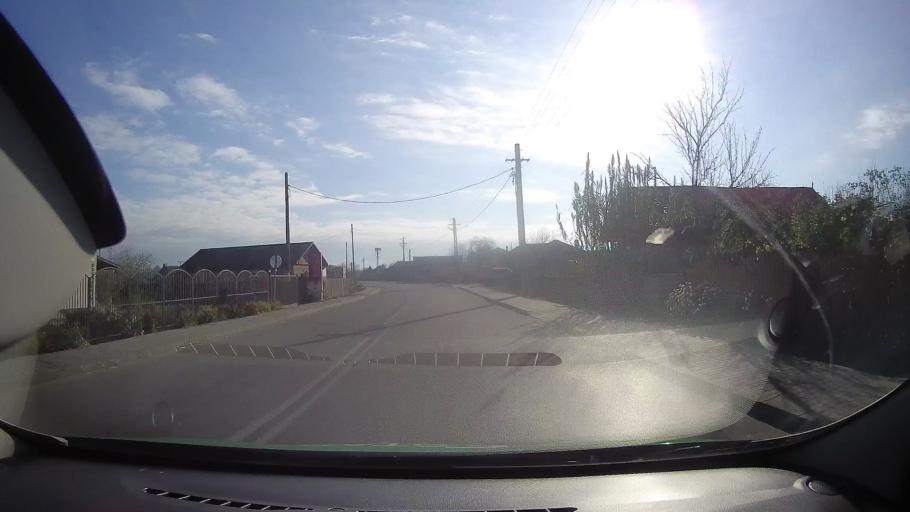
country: RO
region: Tulcea
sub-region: Comuna Murighiol
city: Murighiol
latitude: 45.0383
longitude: 29.1601
